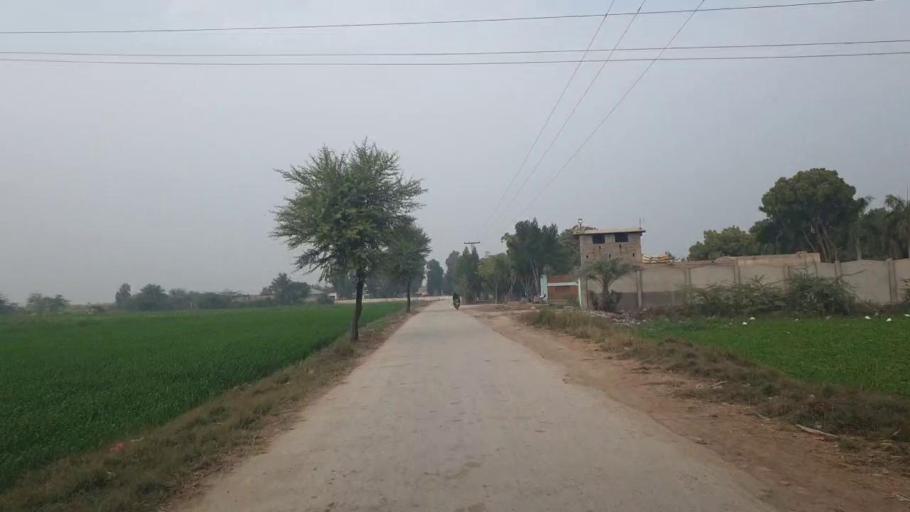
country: PK
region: Sindh
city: Berani
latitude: 25.8107
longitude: 68.7324
